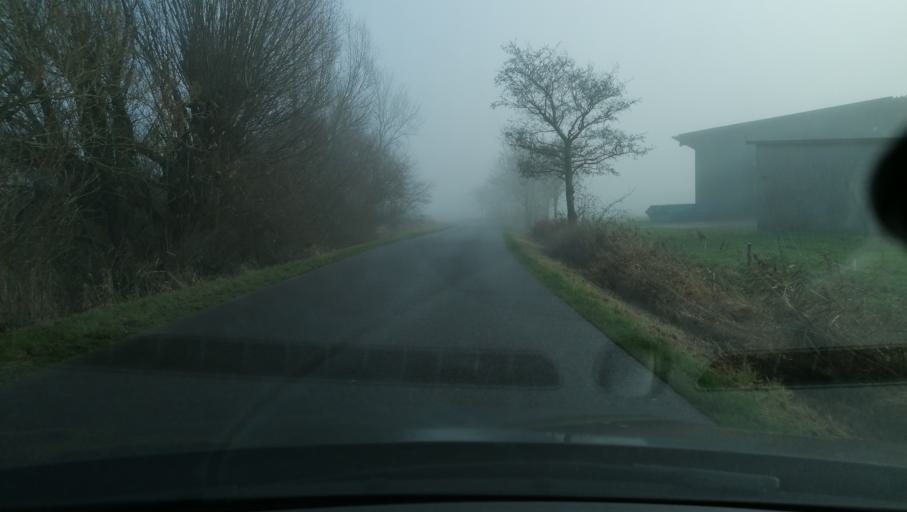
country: DE
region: Schleswig-Holstein
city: Epenwohrden
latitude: 54.1002
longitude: 9.0516
